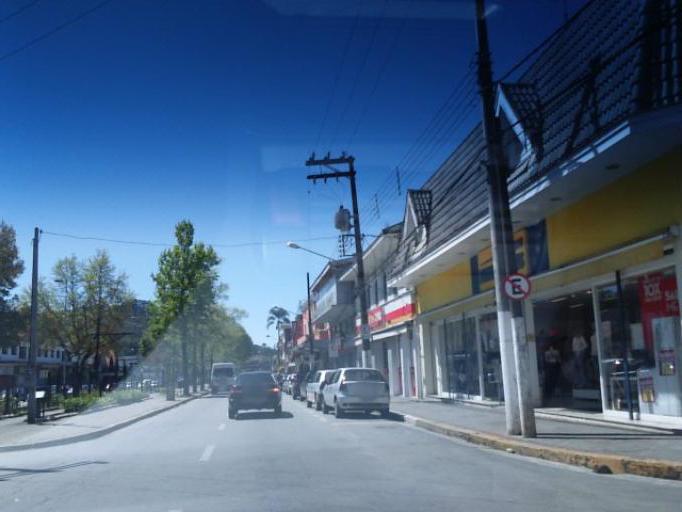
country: BR
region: Sao Paulo
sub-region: Campos Do Jordao
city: Campos do Jordao
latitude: -22.7409
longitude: -45.5943
